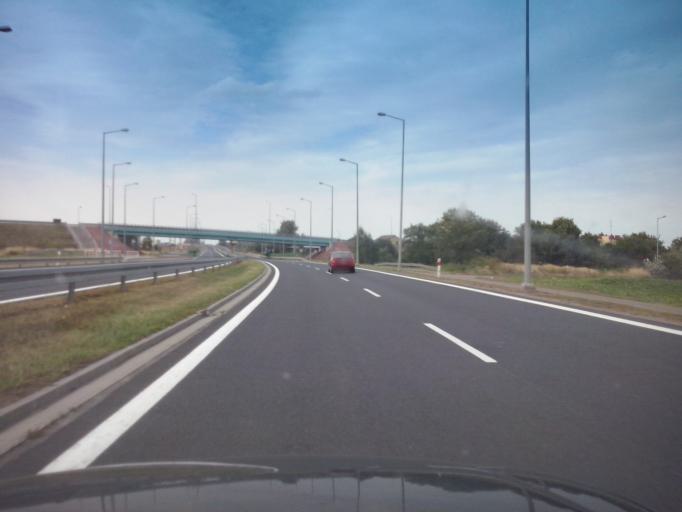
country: PL
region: Subcarpathian Voivodeship
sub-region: Powiat stalowowolski
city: Stalowa Wola
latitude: 50.6053
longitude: 22.0382
